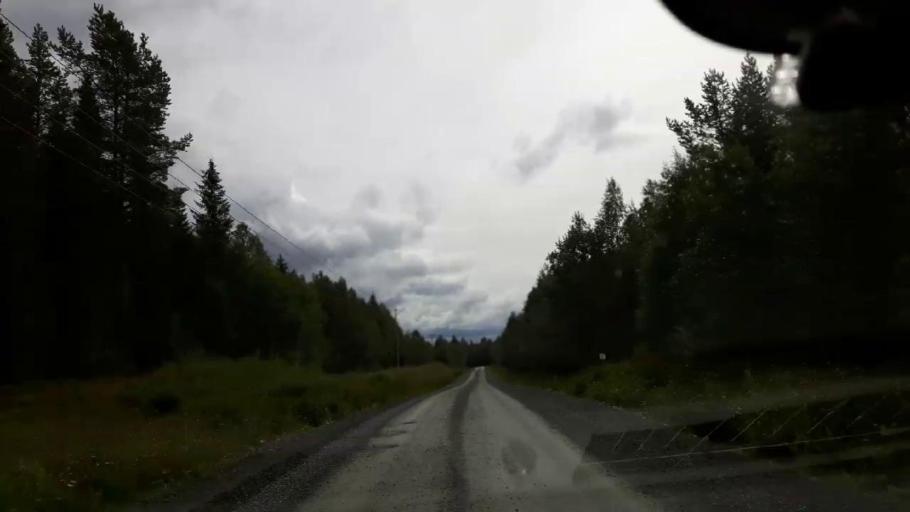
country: SE
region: Jaemtland
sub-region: Krokoms Kommun
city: Valla
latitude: 63.5937
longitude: 14.1414
